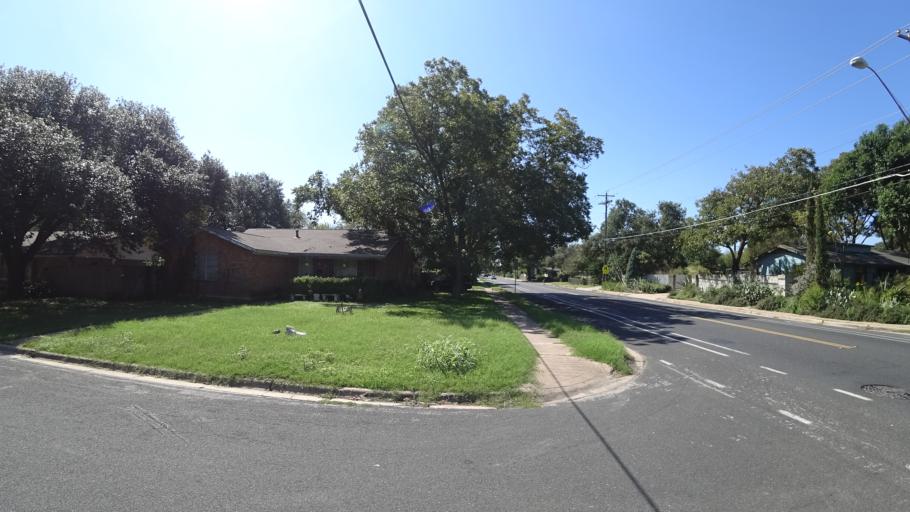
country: US
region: Texas
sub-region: Travis County
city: Austin
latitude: 30.3092
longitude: -97.6954
